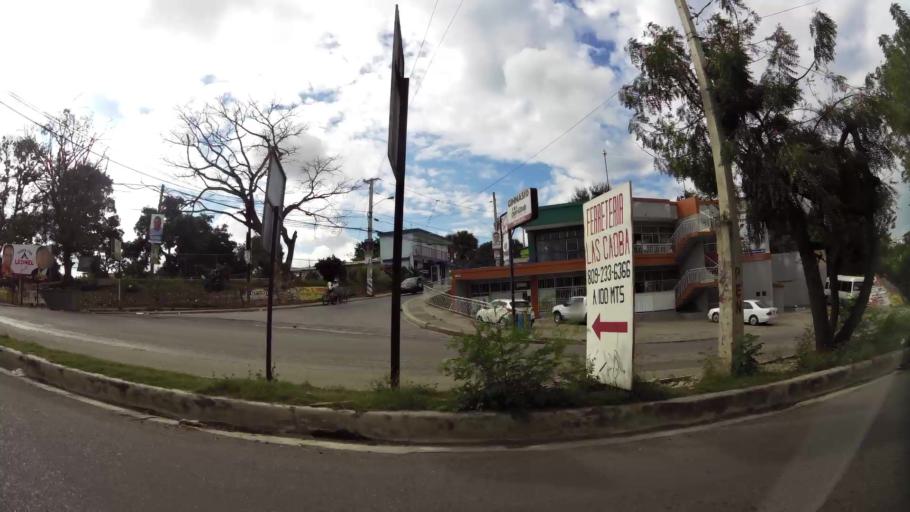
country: DO
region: Santiago
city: Santiago de los Caballeros
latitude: 19.4148
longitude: -70.7092
